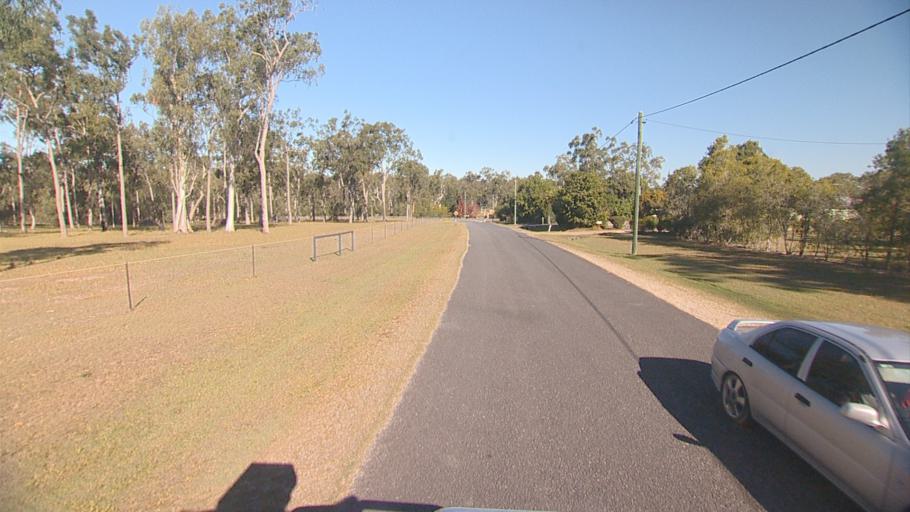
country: AU
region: Queensland
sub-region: Logan
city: Chambers Flat
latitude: -27.7286
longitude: 153.0668
